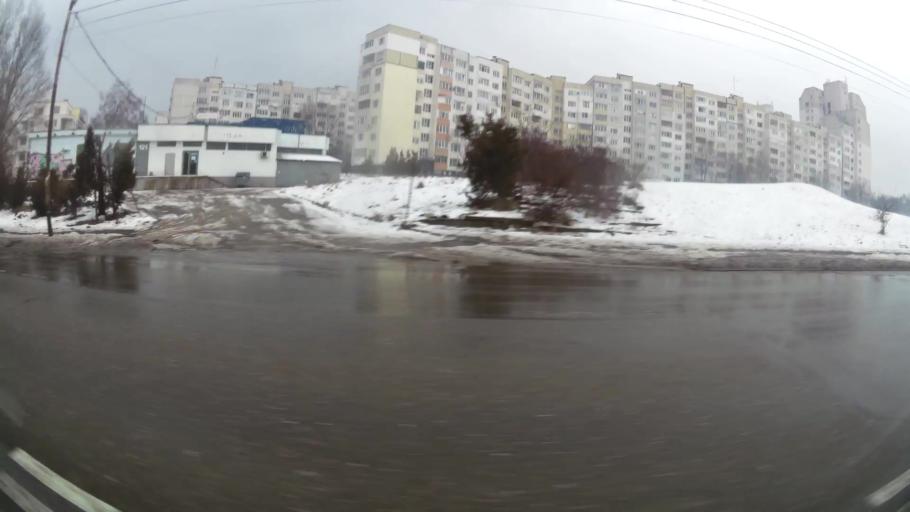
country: BG
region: Sofiya
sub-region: Obshtina Bozhurishte
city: Bozhurishte
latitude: 42.6869
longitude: 23.2397
